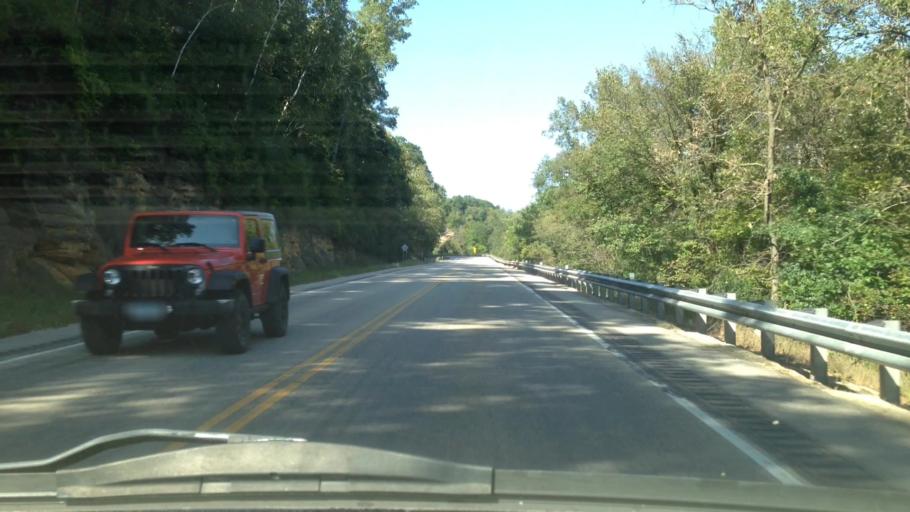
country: US
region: Minnesota
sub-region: Fillmore County
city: Rushford
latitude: 43.8404
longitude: -91.7546
